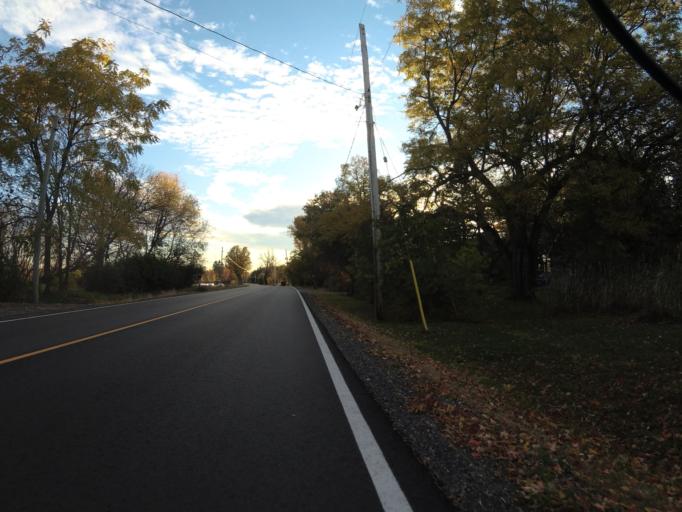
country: CA
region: Ontario
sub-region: Lanark County
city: Smiths Falls
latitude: 44.9608
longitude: -75.8121
